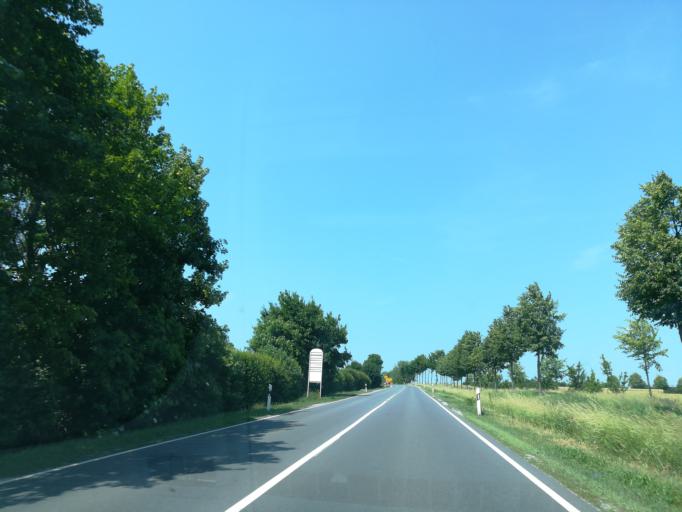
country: DE
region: Saxony-Anhalt
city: Aschersleben
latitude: 51.7766
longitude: 11.4571
